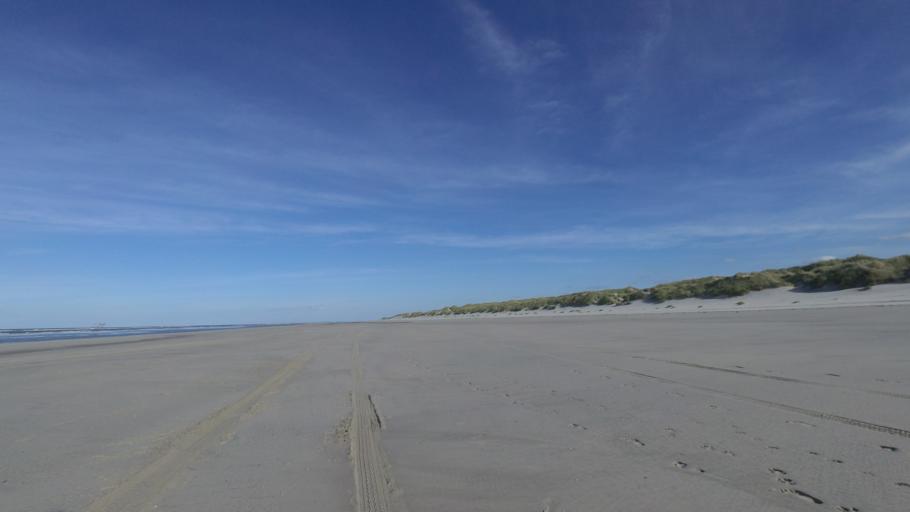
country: NL
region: Friesland
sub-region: Gemeente Dongeradeel
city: Holwerd
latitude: 53.4662
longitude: 5.8756
